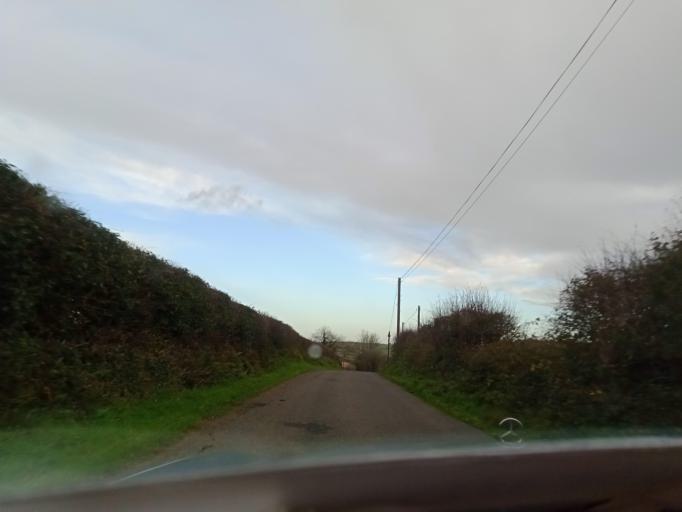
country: IE
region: Munster
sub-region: Waterford
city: Waterford
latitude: 52.3205
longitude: -7.0449
